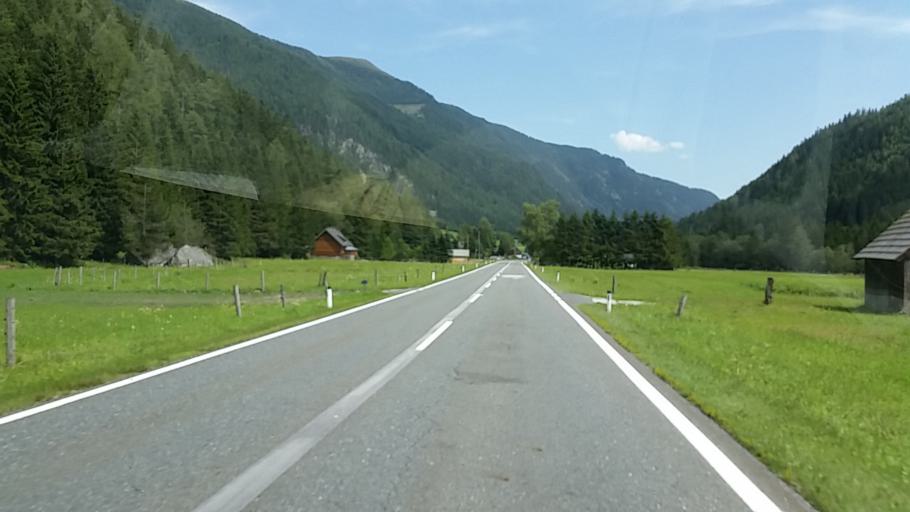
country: AT
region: Salzburg
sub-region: Politischer Bezirk Tamsweg
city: Tweng
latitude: 47.1866
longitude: 13.6083
